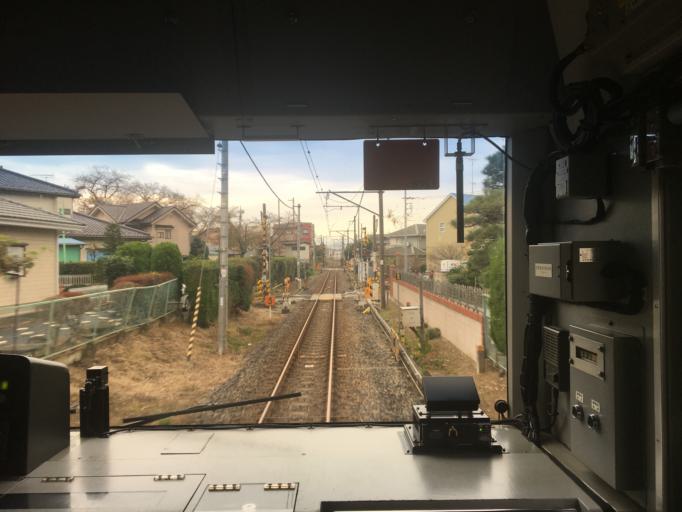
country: JP
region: Saitama
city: Kawagoe
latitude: 35.9190
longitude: 139.4393
